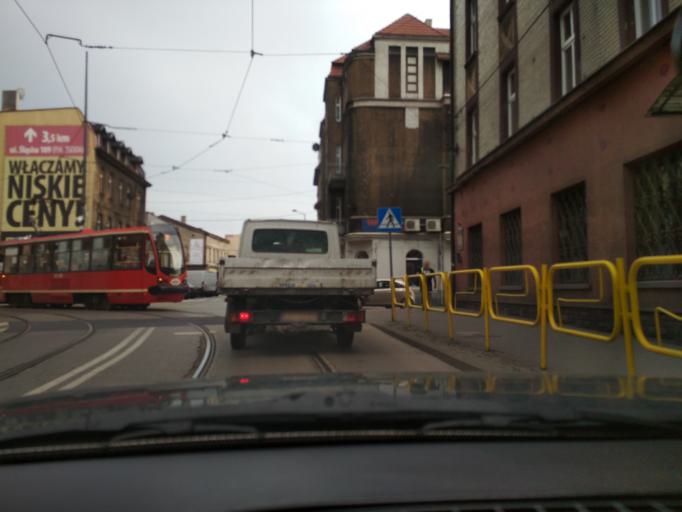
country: PL
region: Silesian Voivodeship
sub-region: Swietochlowice
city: Swietochlowice
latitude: 50.2914
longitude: 18.9156
